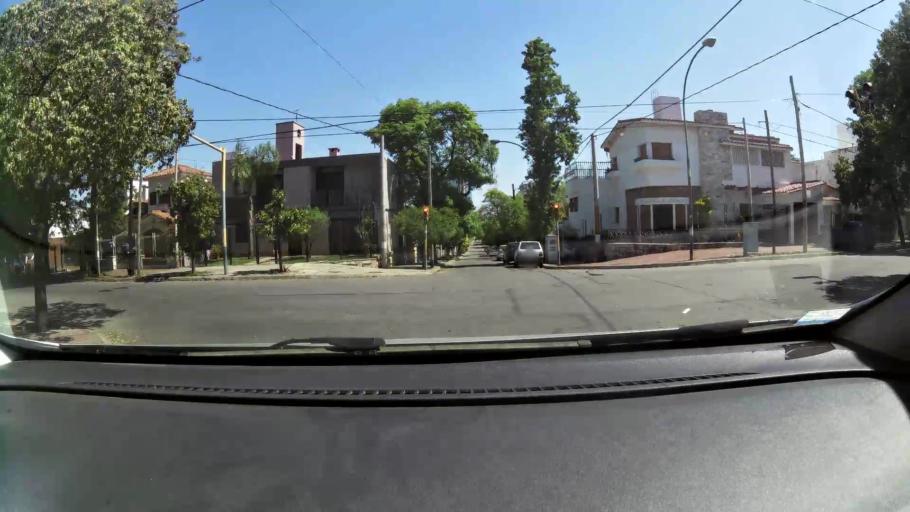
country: AR
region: Cordoba
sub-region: Departamento de Capital
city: Cordoba
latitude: -31.4012
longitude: -64.1881
